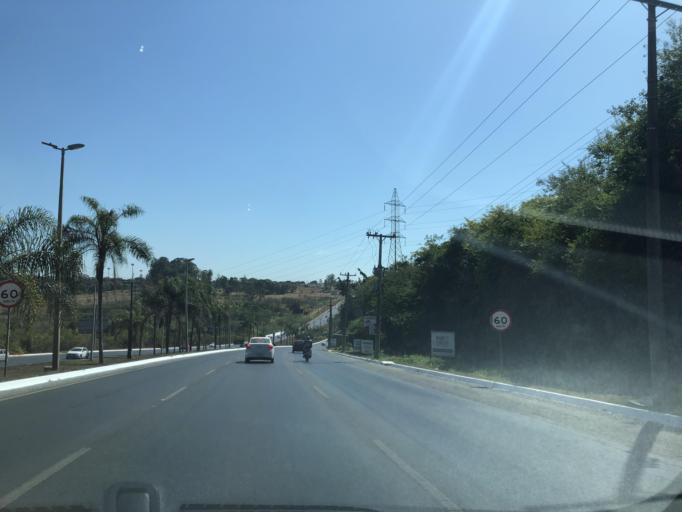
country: BR
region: Federal District
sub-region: Brasilia
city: Brasilia
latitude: -15.8469
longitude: -48.0748
